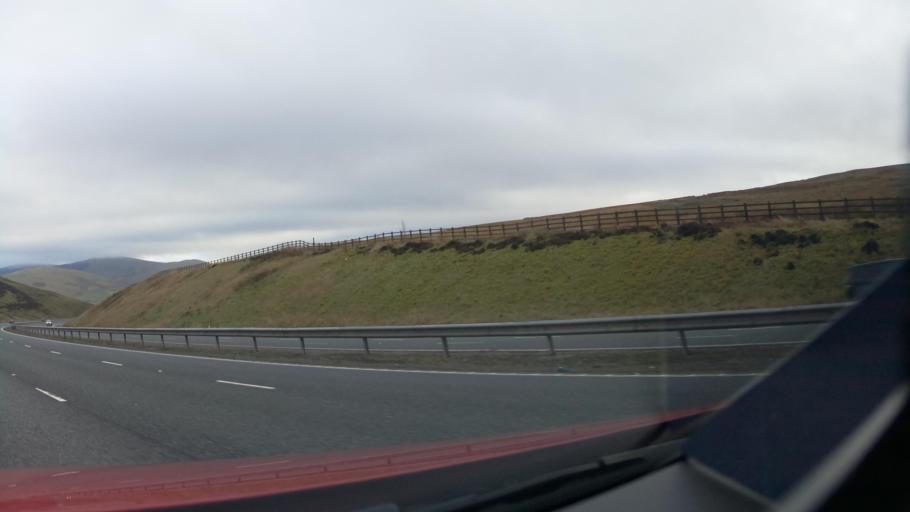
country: GB
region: Scotland
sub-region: South Lanarkshire
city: Douglas
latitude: 55.5210
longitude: -3.7315
